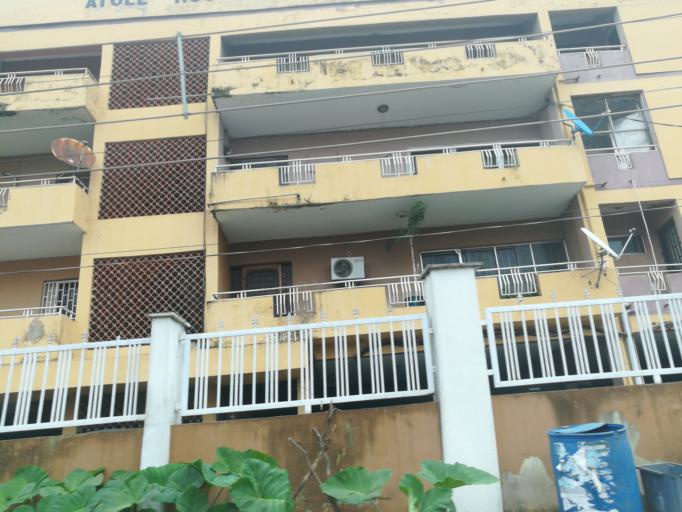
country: NG
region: Lagos
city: Ojota
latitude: 6.5874
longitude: 3.3653
